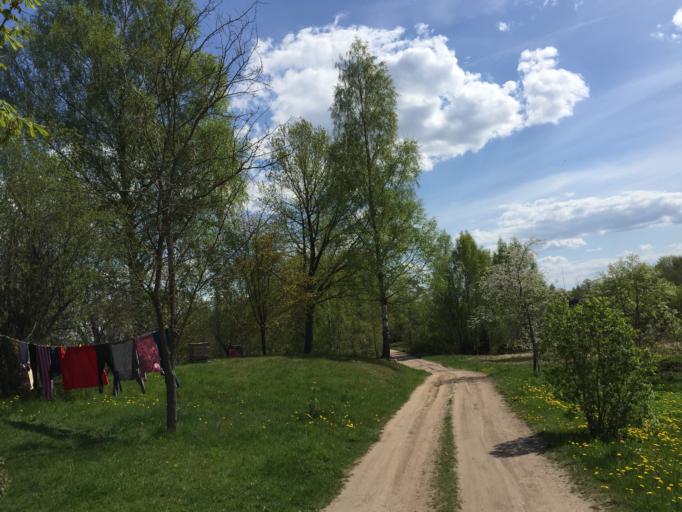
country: LV
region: Limbazu Rajons
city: Limbazi
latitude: 57.3521
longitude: 24.6596
